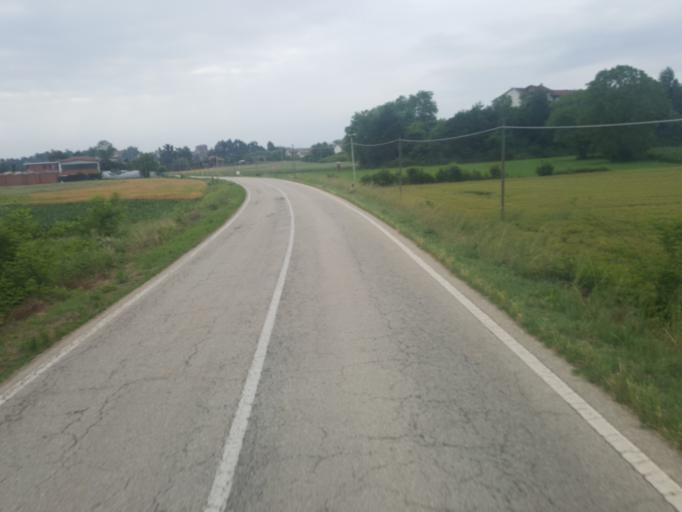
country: IT
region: Piedmont
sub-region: Provincia di Torino
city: Pralormo
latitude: 44.8579
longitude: 7.8795
